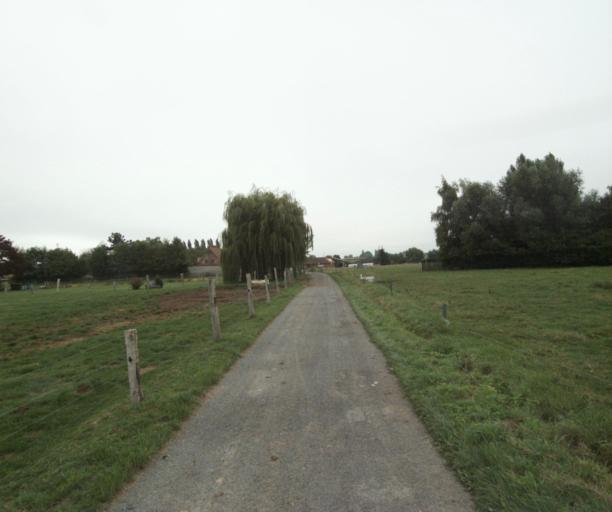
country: FR
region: Nord-Pas-de-Calais
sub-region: Departement du Nord
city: Baisieux
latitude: 50.6051
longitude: 3.2505
